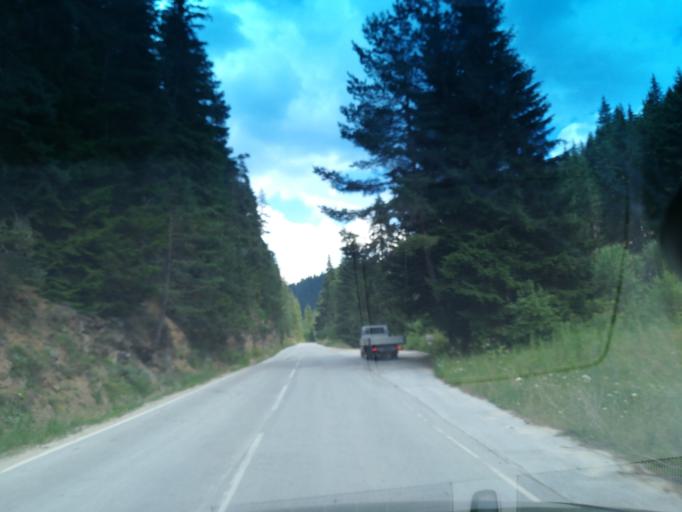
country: BG
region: Smolyan
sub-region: Obshtina Chepelare
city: Chepelare
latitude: 41.6624
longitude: 24.6438
